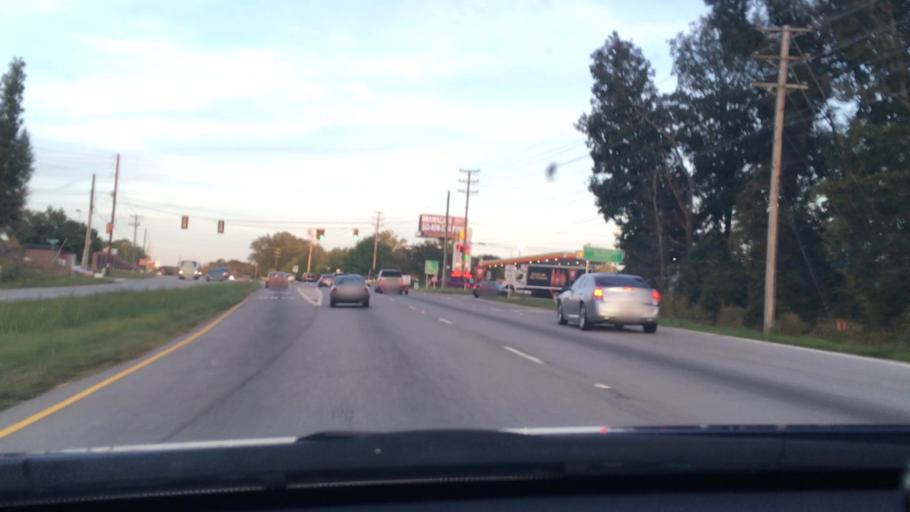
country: US
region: South Carolina
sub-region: Richland County
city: Hopkins
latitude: 33.9445
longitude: -80.8740
